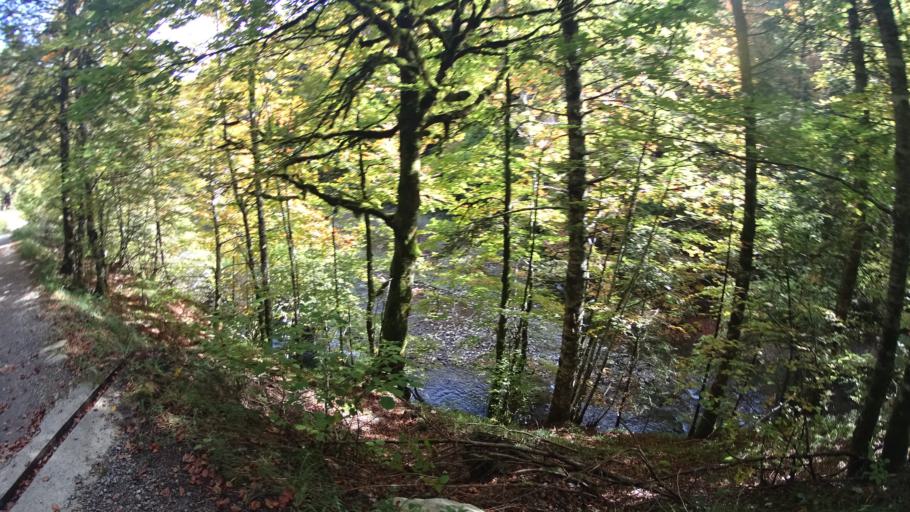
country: ES
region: Navarre
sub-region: Provincia de Navarra
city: Oronz
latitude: 42.9955
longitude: -1.1037
